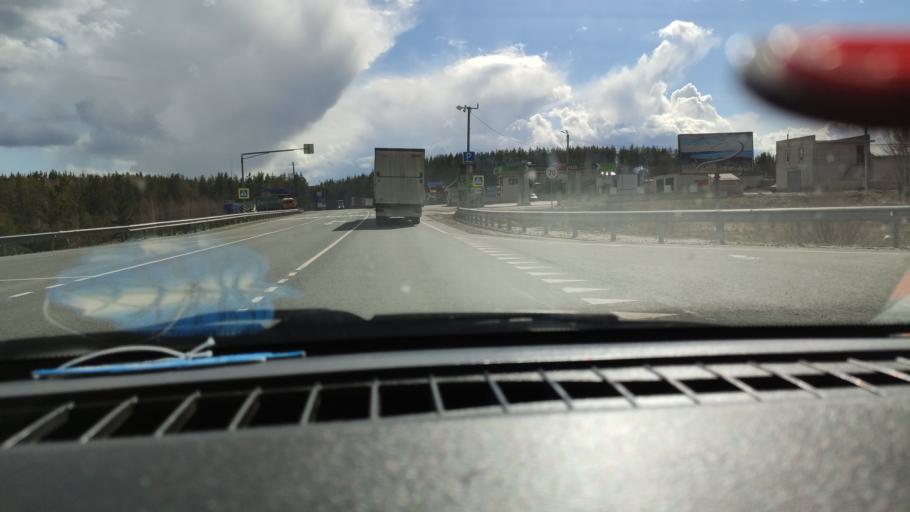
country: RU
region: Saratov
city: Khvalynsk
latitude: 52.5214
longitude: 48.0195
